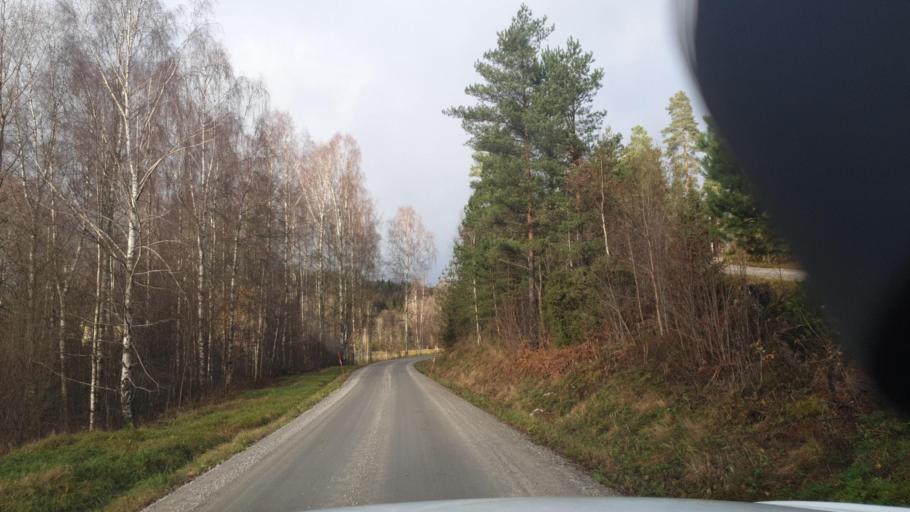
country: SE
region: Vaermland
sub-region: Sunne Kommun
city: Sunne
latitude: 59.7041
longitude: 12.8861
